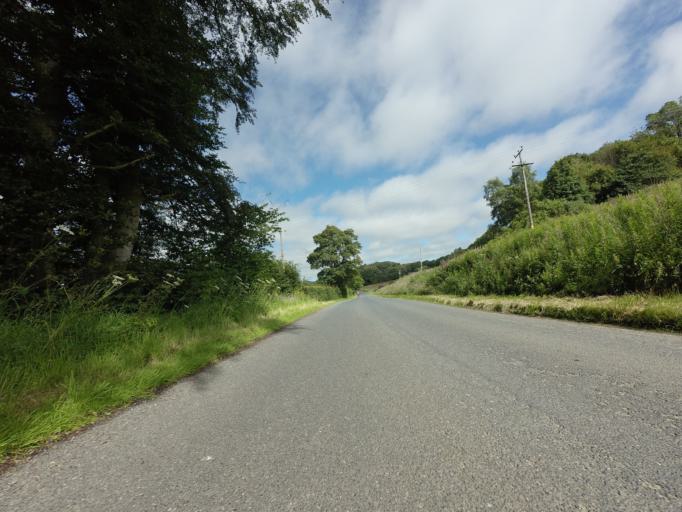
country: GB
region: Scotland
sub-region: Aberdeenshire
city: Turriff
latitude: 57.5440
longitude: -2.4790
